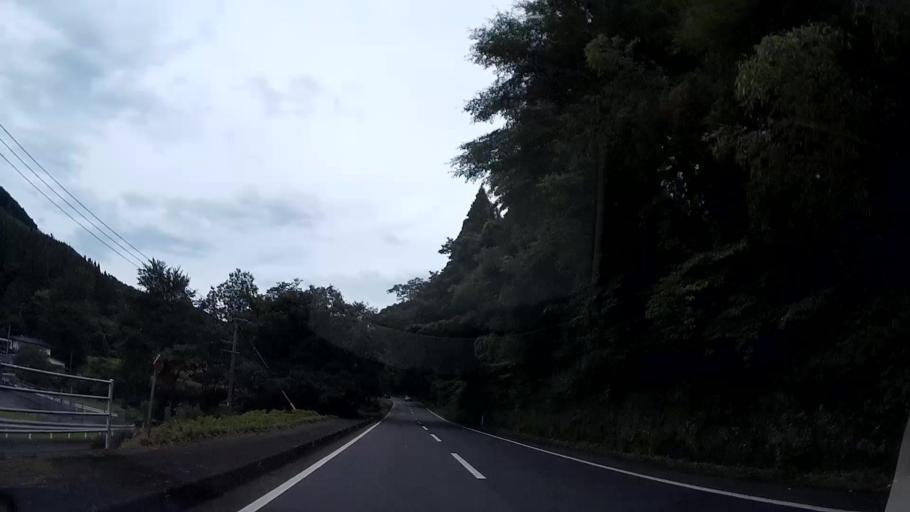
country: JP
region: Oita
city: Hita
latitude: 33.1264
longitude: 130.9989
